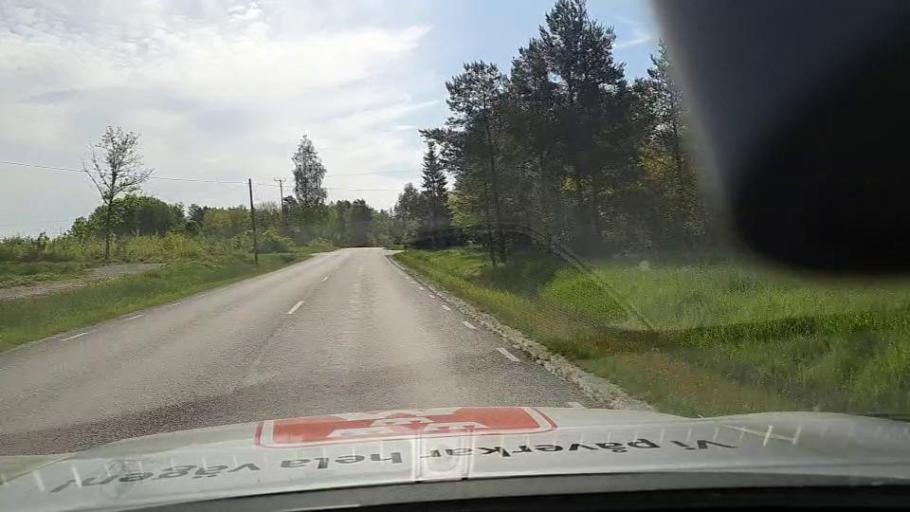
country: SE
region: Soedermanland
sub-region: Eskilstuna Kommun
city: Eskilstuna
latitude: 59.3189
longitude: 16.5649
